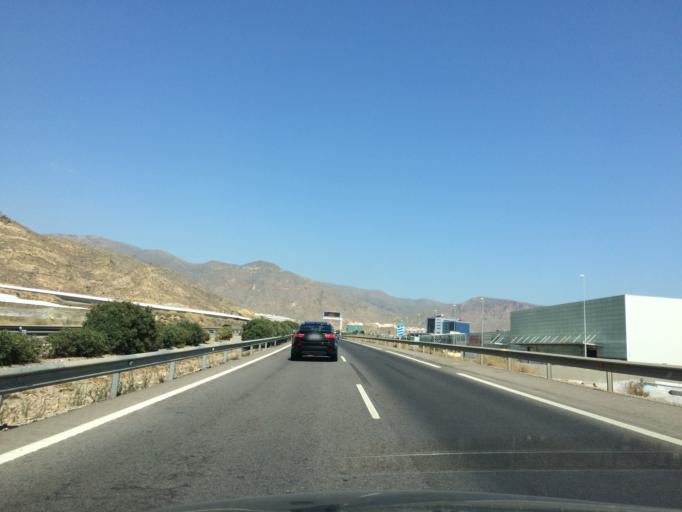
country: ES
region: Andalusia
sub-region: Provincia de Almeria
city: Aguadulce
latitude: 36.8153
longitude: -2.6047
